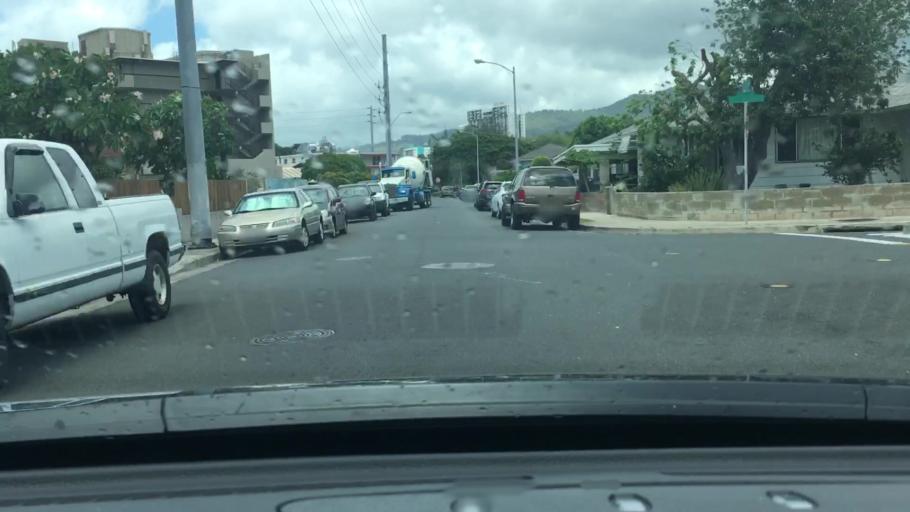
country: US
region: Hawaii
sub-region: Honolulu County
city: Honolulu
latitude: 21.2748
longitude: -157.8146
